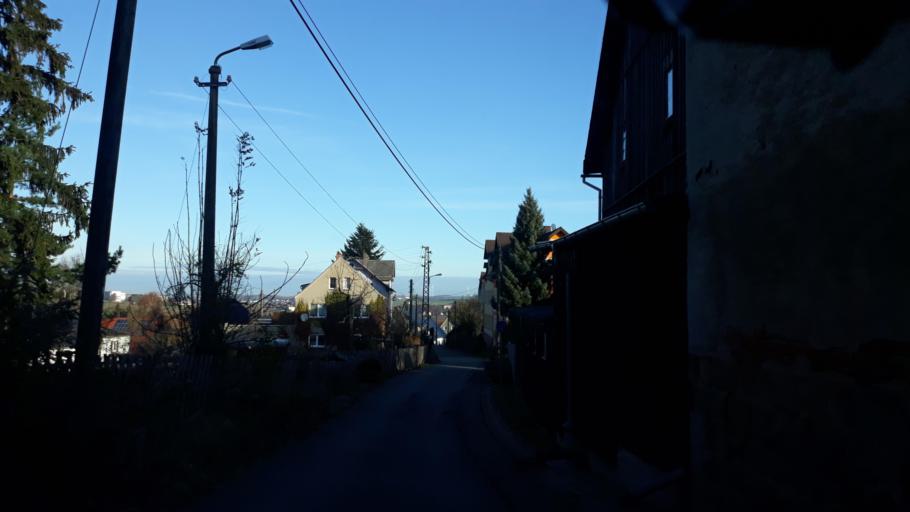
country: DE
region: Saxony
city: Wilkau-Hasslau
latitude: 50.6563
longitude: 12.5091
